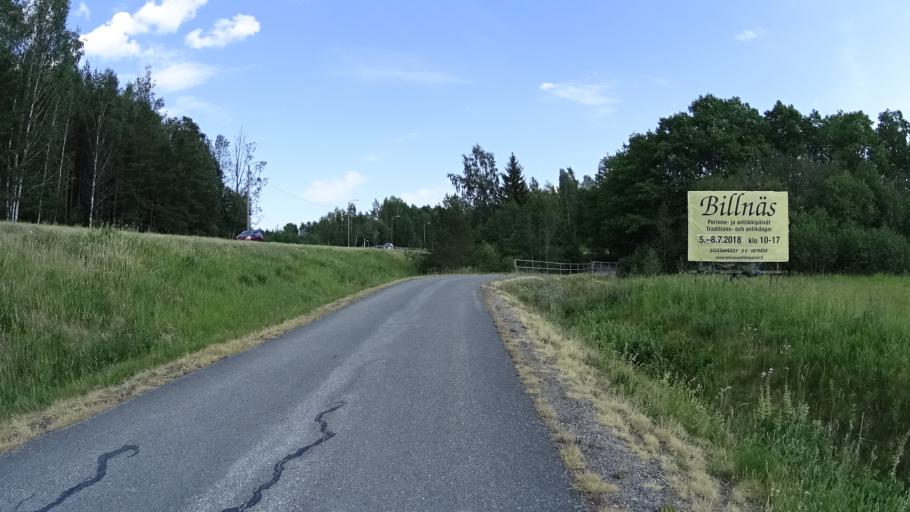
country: FI
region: Uusimaa
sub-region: Raaseporin
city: Karis
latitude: 60.0950
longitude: 23.6258
